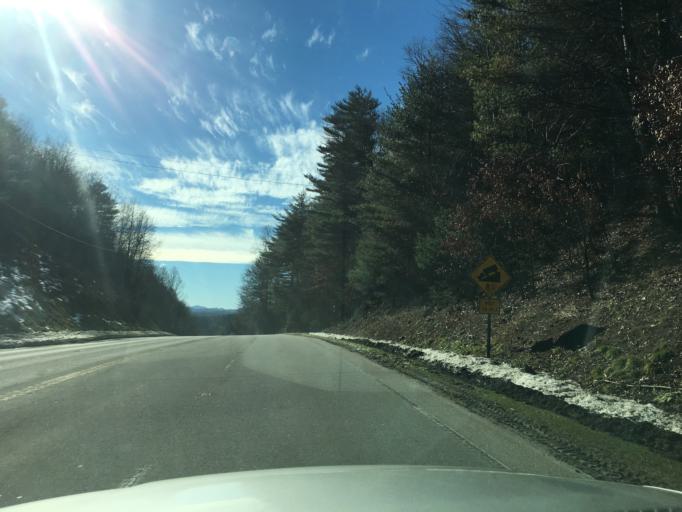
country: US
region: North Carolina
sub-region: Transylvania County
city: Brevard
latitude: 35.2960
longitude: -82.6811
